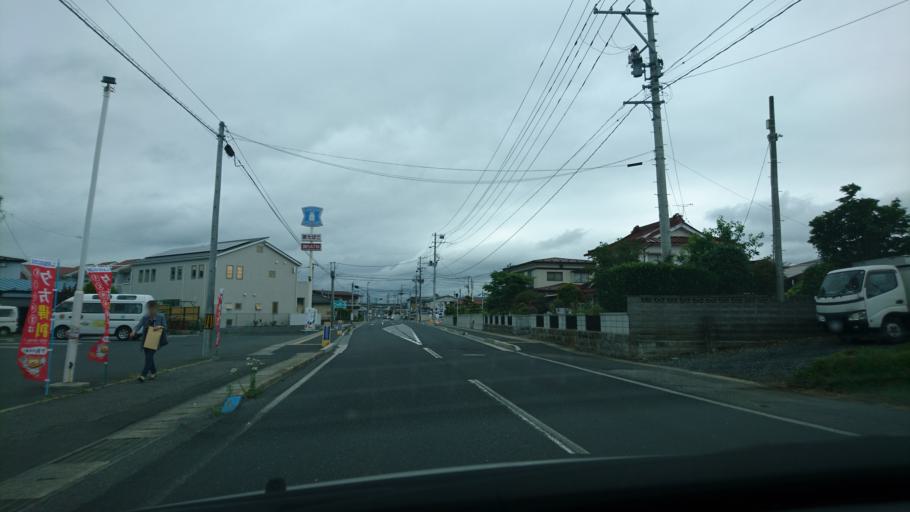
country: JP
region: Iwate
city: Ichinoseki
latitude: 38.9294
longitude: 141.1487
